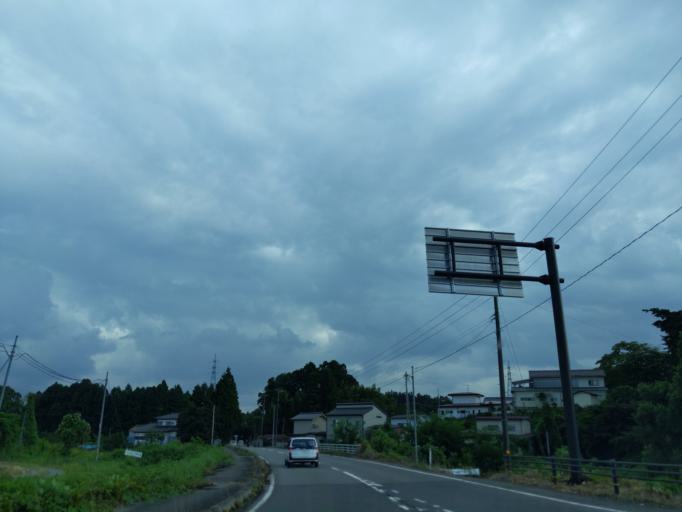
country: JP
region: Fukushima
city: Sukagawa
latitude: 37.3257
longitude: 140.3265
